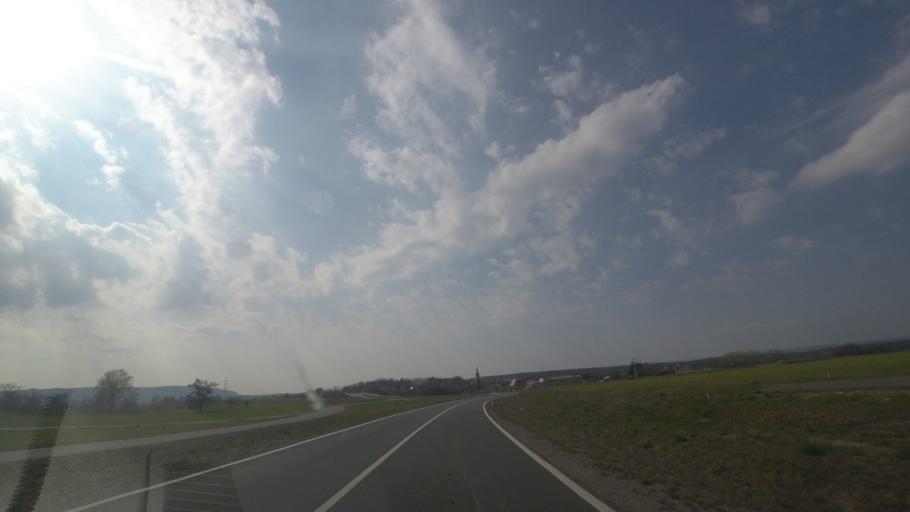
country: DE
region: Bavaria
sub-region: Regierungsbezirk Unterfranken
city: Castell
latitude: 49.7651
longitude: 10.3525
